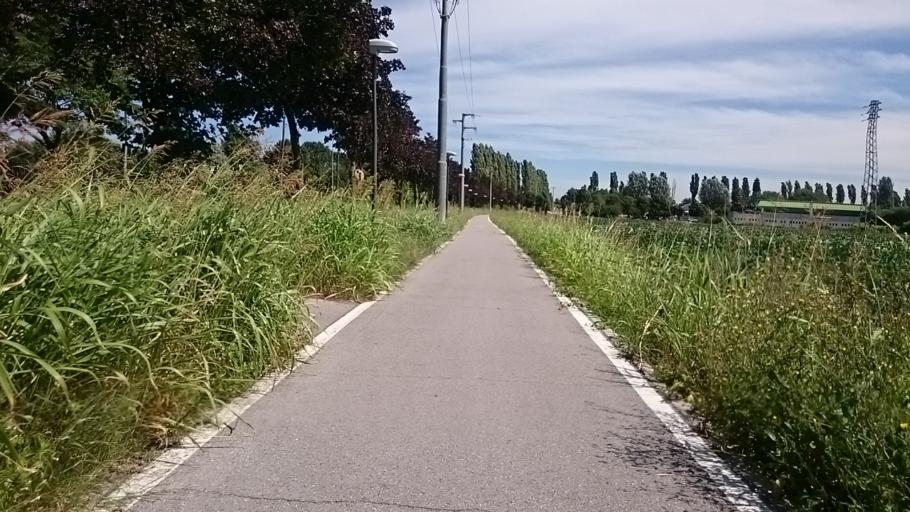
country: IT
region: Veneto
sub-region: Provincia di Padova
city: Vigonza
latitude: 45.4378
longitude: 11.9645
